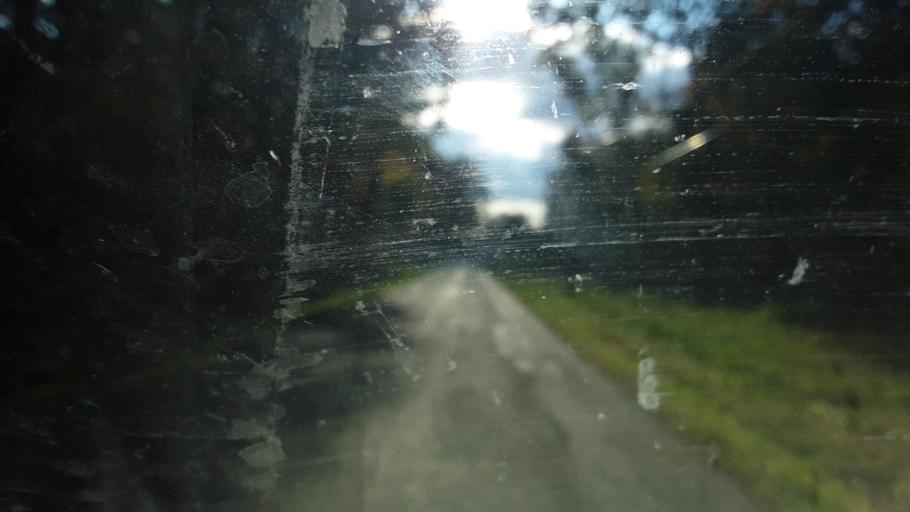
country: US
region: Ohio
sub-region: Knox County
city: Fredericktown
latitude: 40.4866
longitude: -82.5201
